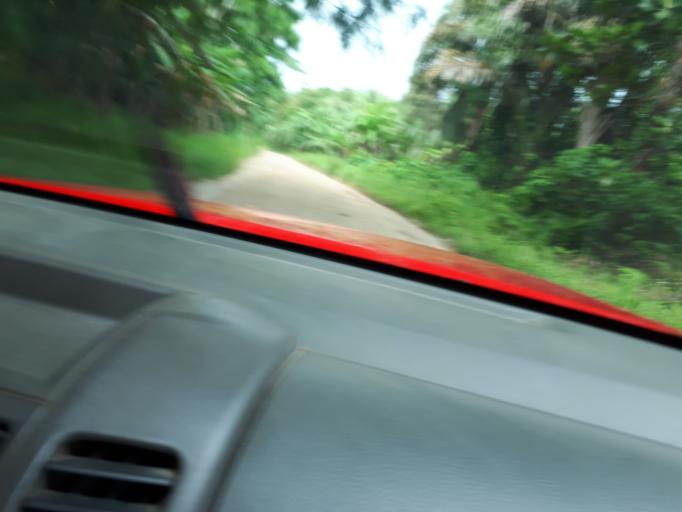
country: VU
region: Sanma
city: Luganville
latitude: -15.5703
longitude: 166.9462
